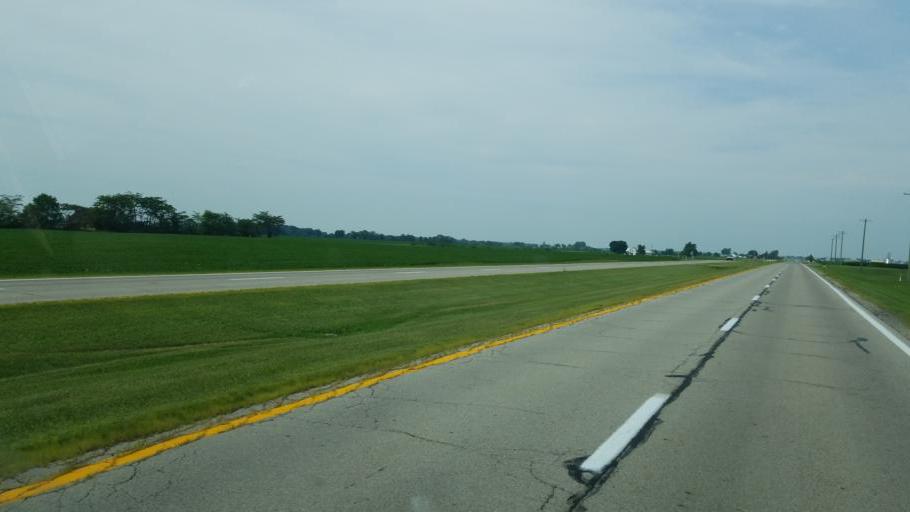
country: US
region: Ohio
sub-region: Madison County
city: London
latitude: 39.9371
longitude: -83.4228
